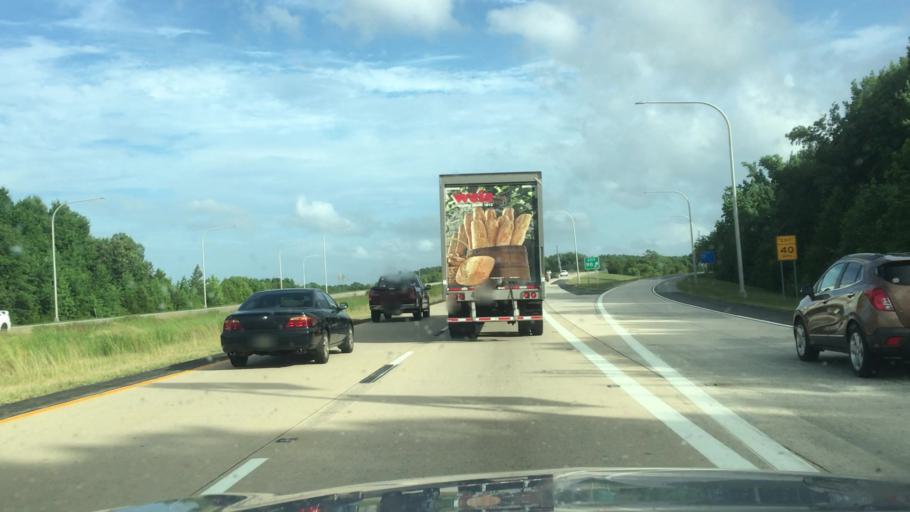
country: US
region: Delaware
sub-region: Kent County
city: Dover
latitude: 39.1707
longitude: -75.4955
